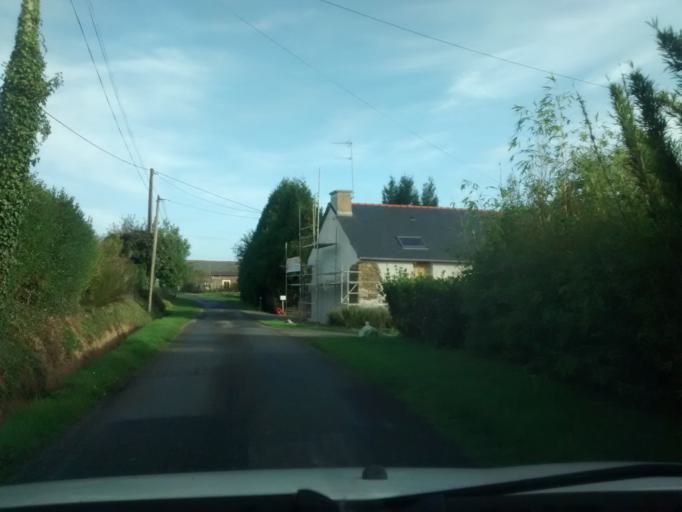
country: FR
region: Brittany
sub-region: Departement d'Ille-et-Vilaine
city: Brece
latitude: 48.1276
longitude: -1.4919
